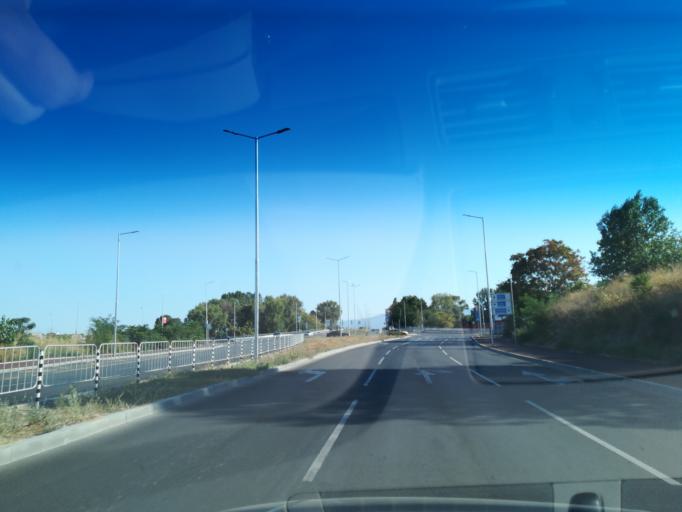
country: BG
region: Plovdiv
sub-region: Obshtina Plovdiv
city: Plovdiv
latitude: 42.1613
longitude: 24.7644
